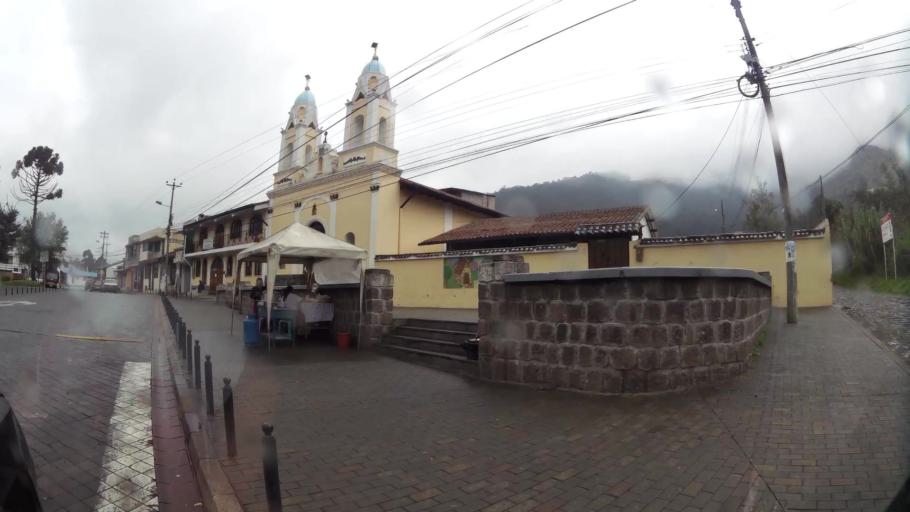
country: EC
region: Pichincha
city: Sangolqui
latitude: -0.2858
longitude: -78.4410
